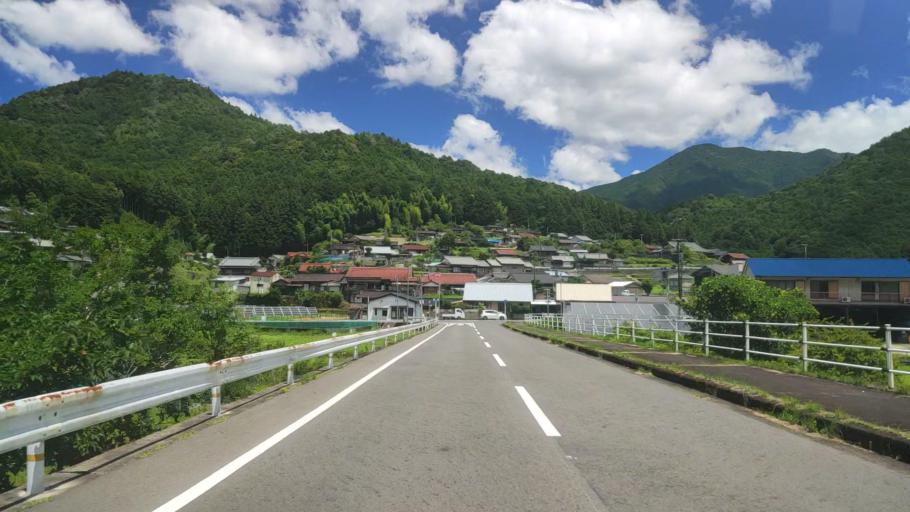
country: JP
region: Mie
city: Owase
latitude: 33.9834
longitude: 136.0399
